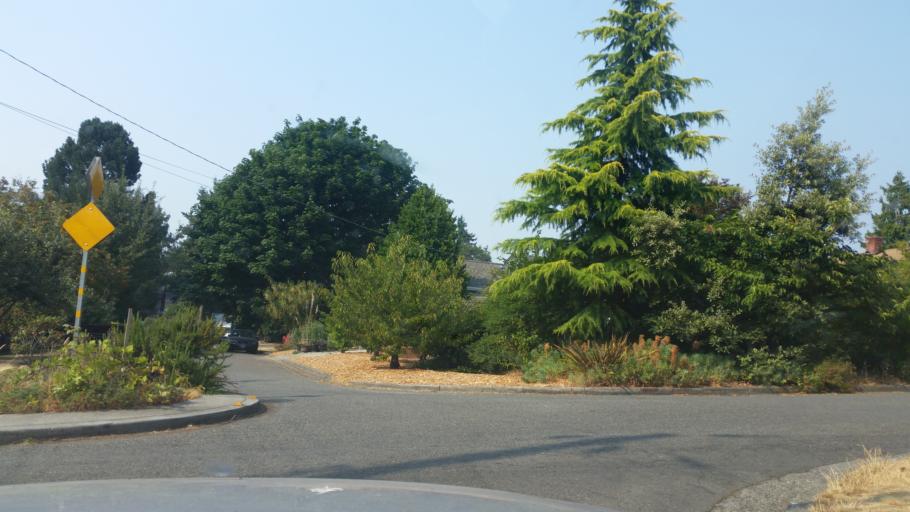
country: US
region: Washington
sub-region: King County
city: Shoreline
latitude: 47.7014
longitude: -122.3581
